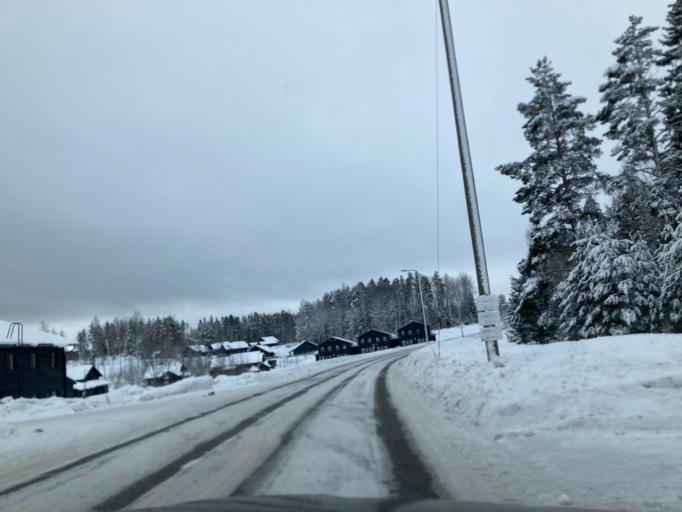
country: FI
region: Central Finland
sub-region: Jaemsae
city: Jaemsae
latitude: 61.8777
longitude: 25.2799
